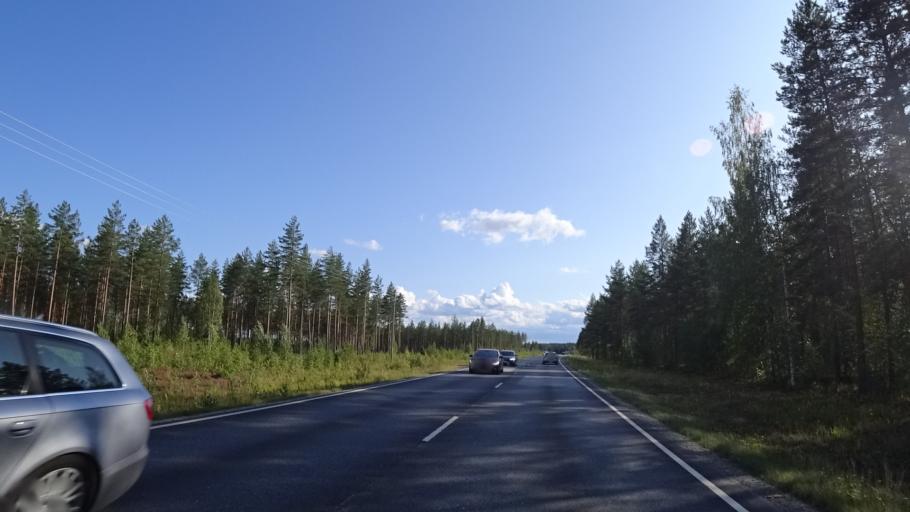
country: FI
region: North Karelia
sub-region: Keski-Karjala
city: Kesaelahti
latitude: 62.0146
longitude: 29.8889
